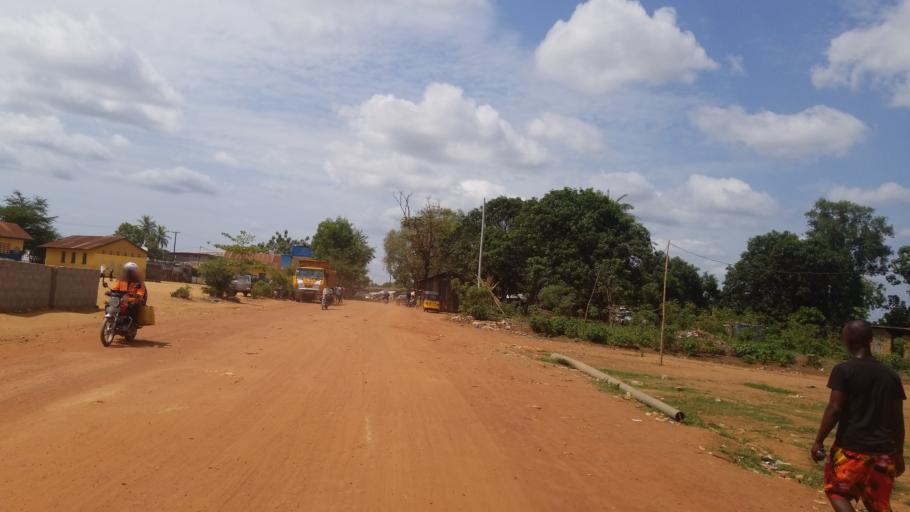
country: SL
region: Western Area
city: Waterloo
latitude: 8.3251
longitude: -13.0638
